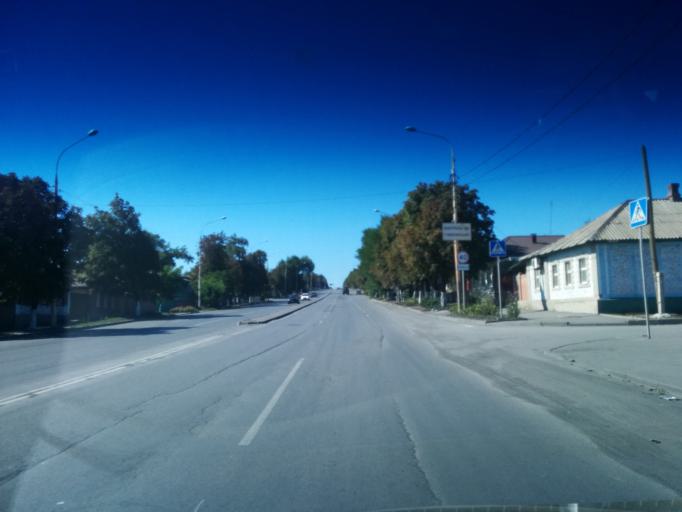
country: RU
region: Rostov
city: Shakhty
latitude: 47.6987
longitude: 40.2366
